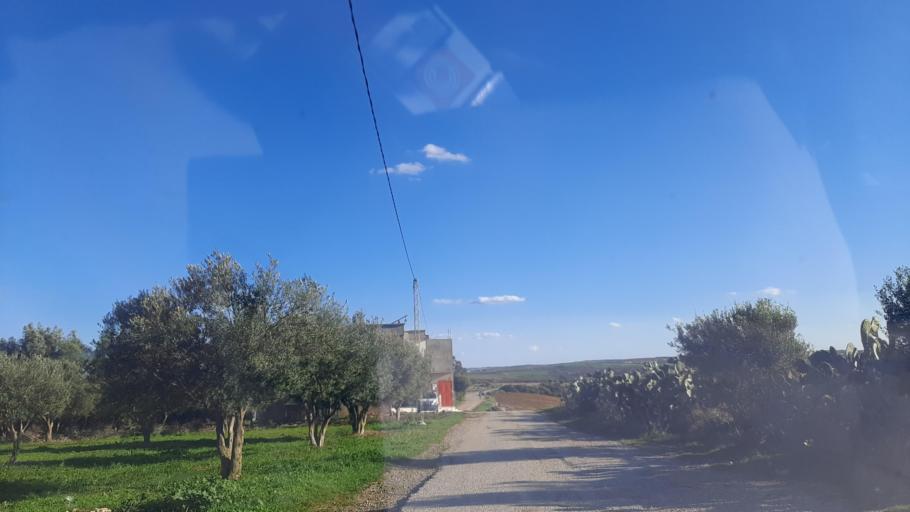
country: TN
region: Nabul
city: El Mida
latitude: 36.8376
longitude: 10.8318
